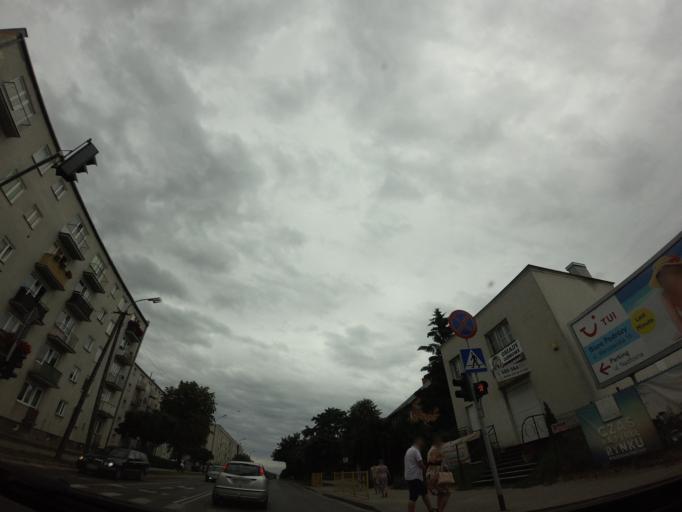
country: PL
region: Masovian Voivodeship
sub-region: Powiat ciechanowski
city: Ciechanow
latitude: 52.8769
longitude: 20.6193
